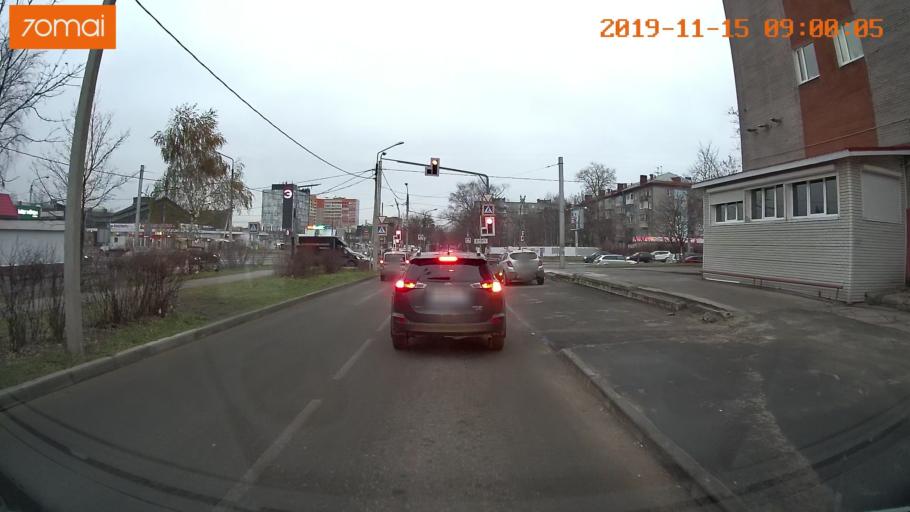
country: RU
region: Vologda
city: Cherepovets
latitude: 59.1299
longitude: 37.9248
